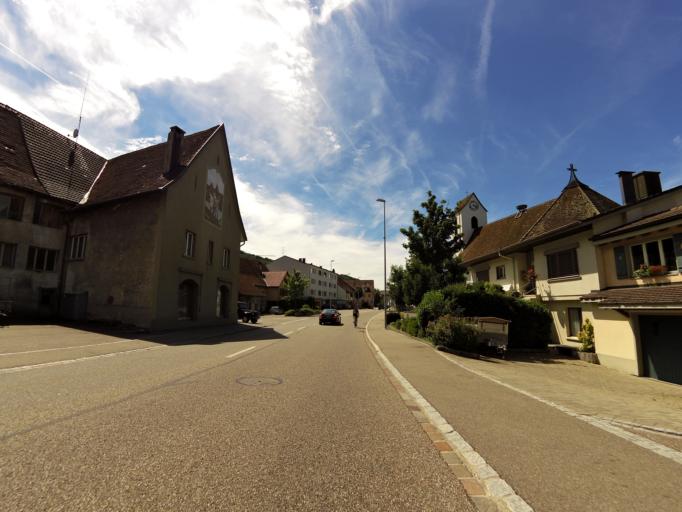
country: CH
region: Aargau
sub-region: Bezirk Rheinfelden
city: Mumpf
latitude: 47.5456
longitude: 7.9235
